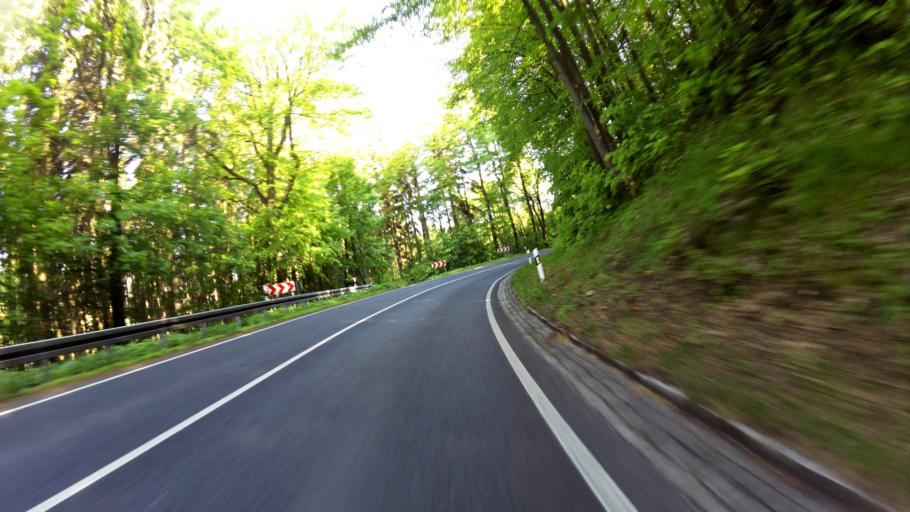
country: DE
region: Saxony
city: Sebnitz
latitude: 50.9886
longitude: 14.2409
